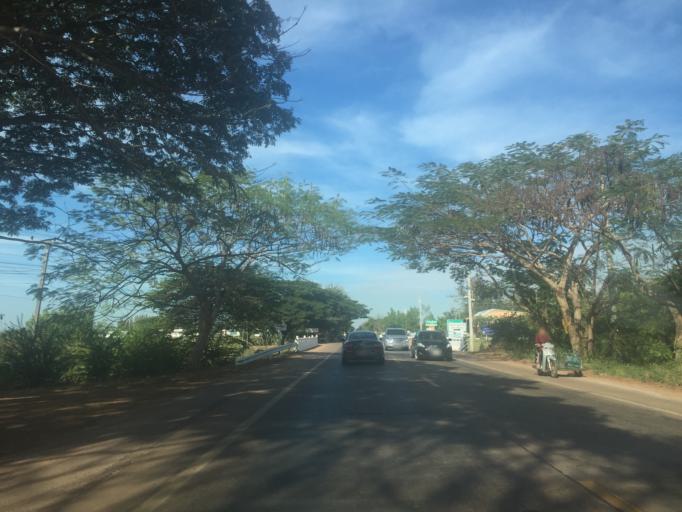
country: TH
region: Changwat Udon Thani
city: Kumphawapi
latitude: 17.1135
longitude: 103.0020
